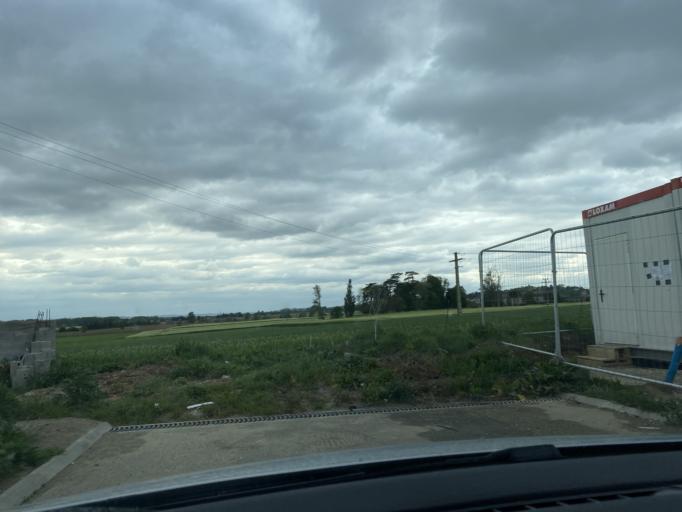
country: FR
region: Midi-Pyrenees
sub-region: Departement de la Haute-Garonne
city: Villefranche-de-Lauragais
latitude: 43.4141
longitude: 1.7119
